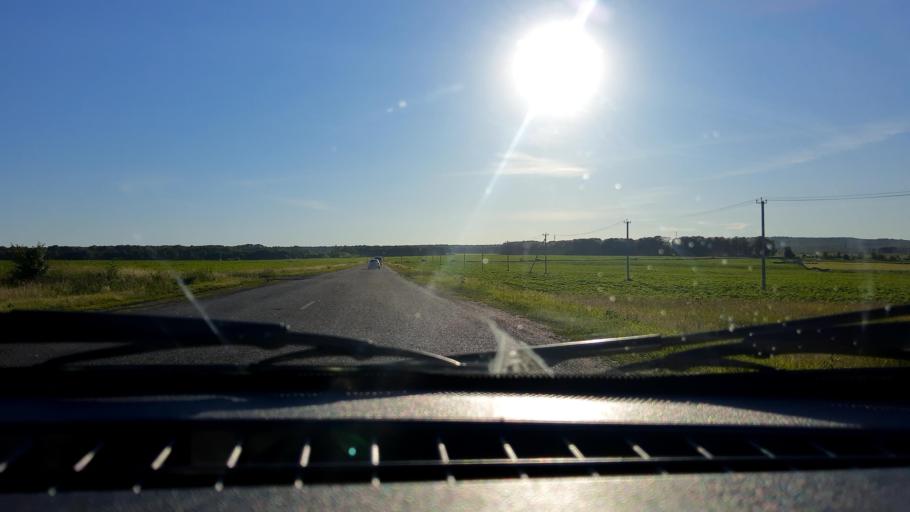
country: RU
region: Bashkortostan
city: Mikhaylovka
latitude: 54.8172
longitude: 55.7767
